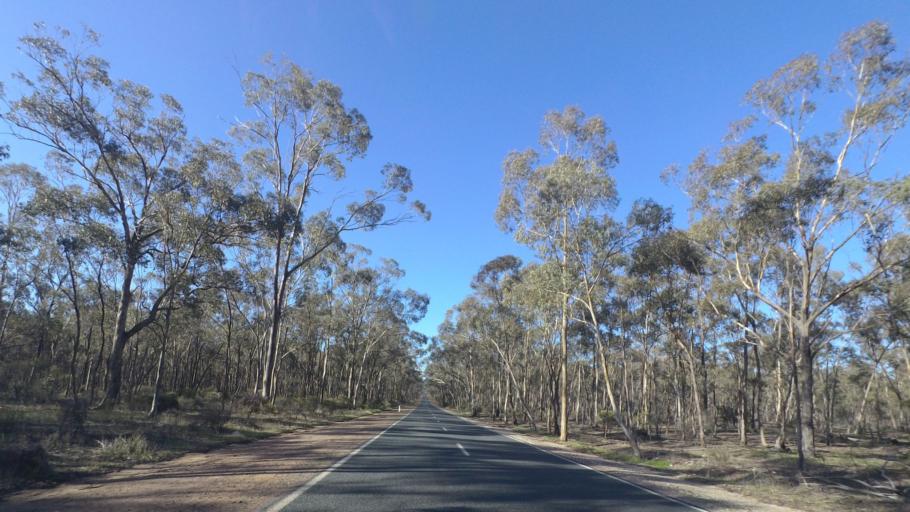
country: AU
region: Victoria
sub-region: Greater Bendigo
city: Epsom
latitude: -36.6724
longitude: 144.4085
